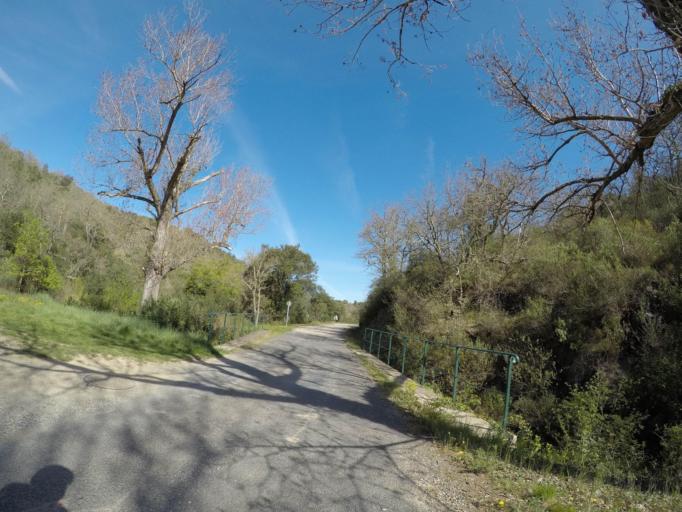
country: FR
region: Languedoc-Roussillon
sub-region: Departement des Pyrenees-Orientales
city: Thuir
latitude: 42.6252
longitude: 2.7043
